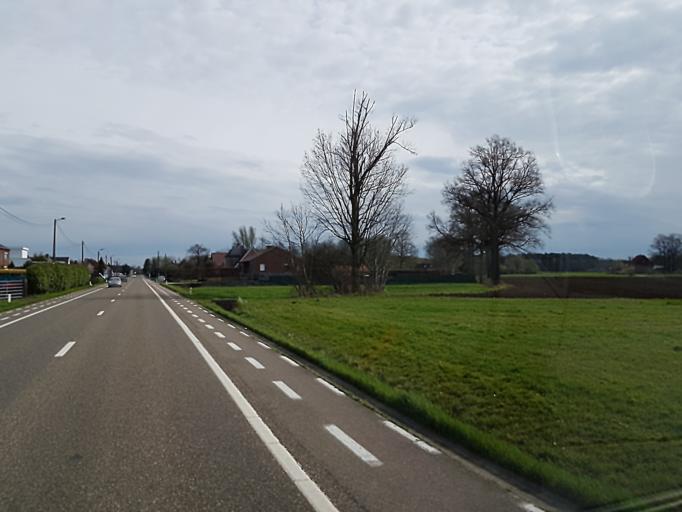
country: BE
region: Flanders
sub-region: Provincie Antwerpen
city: Herselt
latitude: 51.0400
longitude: 4.8582
